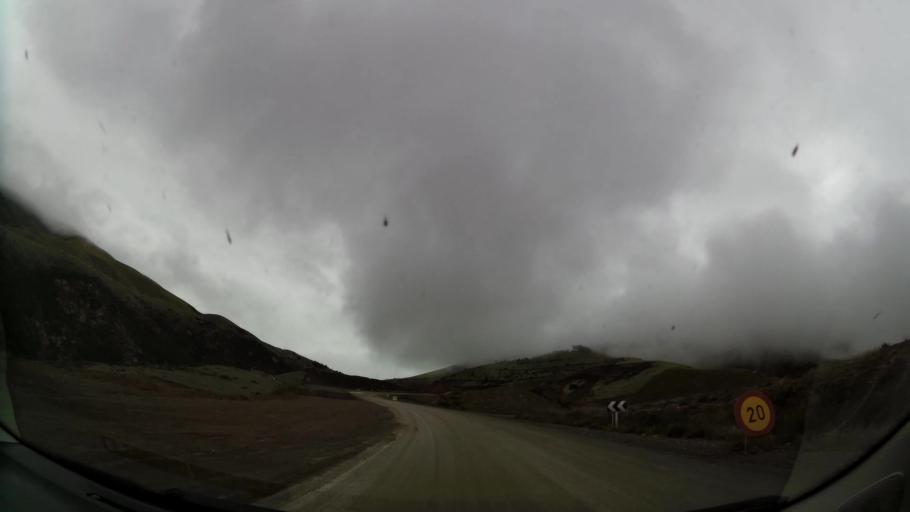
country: MA
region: Taza-Al Hoceima-Taounate
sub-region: Taza
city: Ajdir
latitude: 34.9120
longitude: -3.7968
